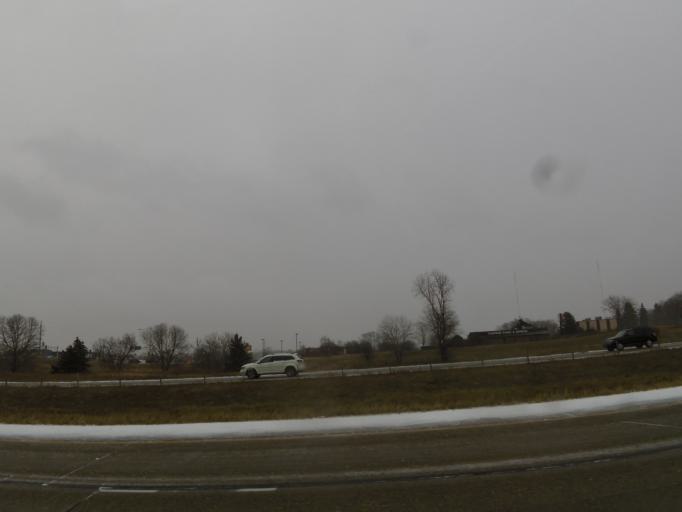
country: US
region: Minnesota
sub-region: Dakota County
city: Eagan
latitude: 44.7892
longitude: -93.2214
